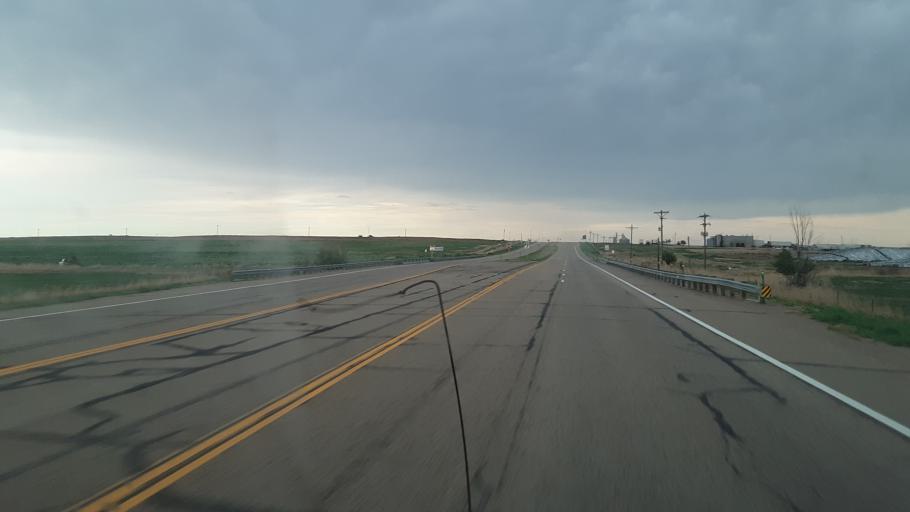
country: US
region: Colorado
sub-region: Prowers County
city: Lamar
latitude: 38.1138
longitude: -102.7391
